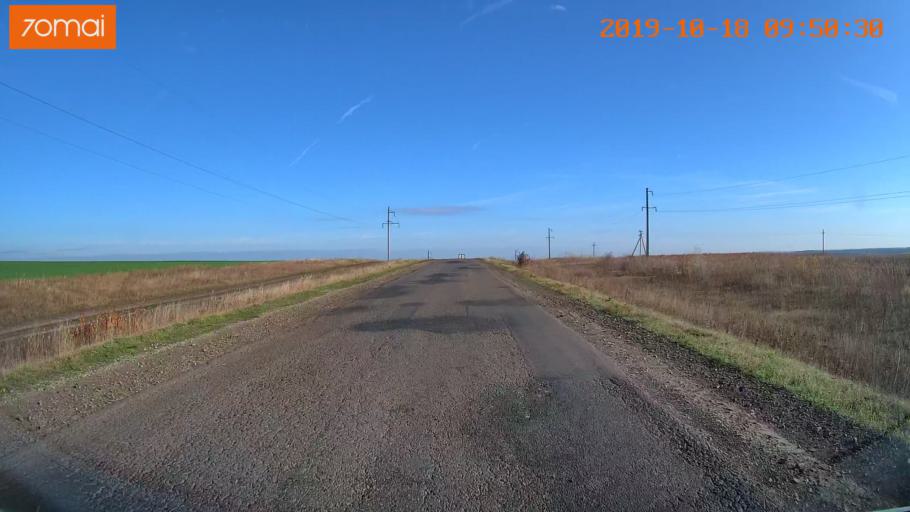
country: RU
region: Tula
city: Kazachka
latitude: 53.3295
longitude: 38.2783
